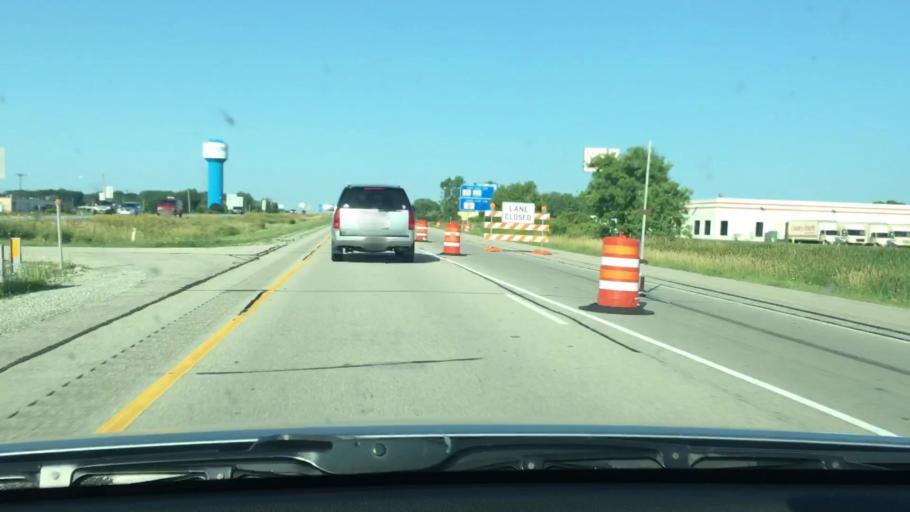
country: US
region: Wisconsin
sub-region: Outagamie County
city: Kaukauna
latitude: 44.3026
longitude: -88.2610
